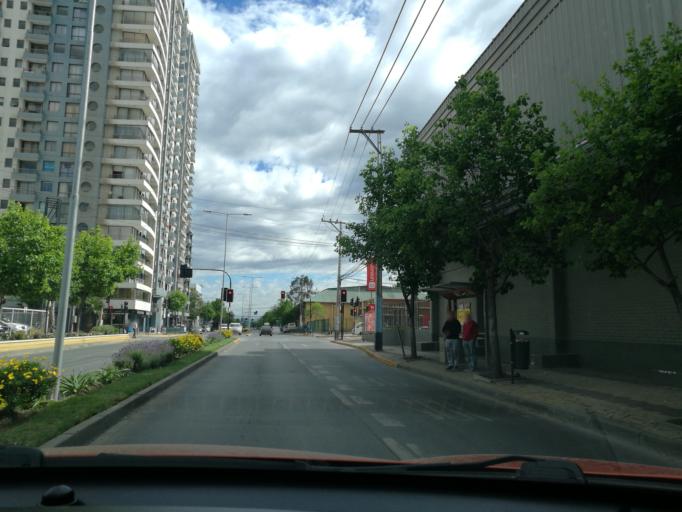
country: CL
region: O'Higgins
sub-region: Provincia de Cachapoal
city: Rancagua
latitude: -34.1716
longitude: -70.7352
